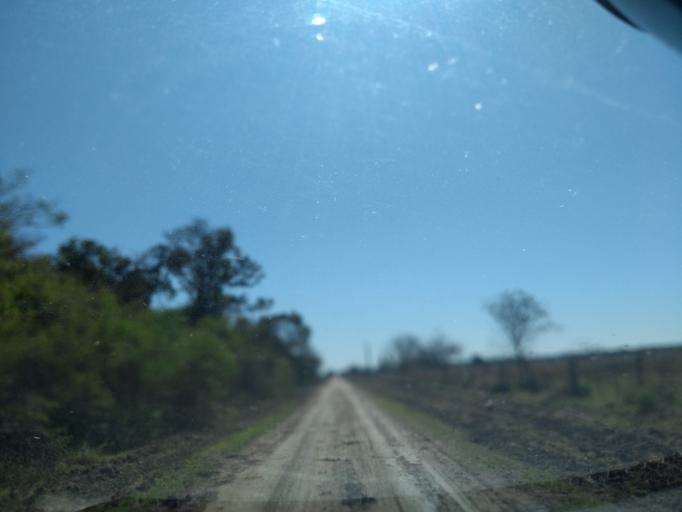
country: AR
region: Chaco
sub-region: Departamento de Quitilipi
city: Quitilipi
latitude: -26.7133
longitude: -60.2241
